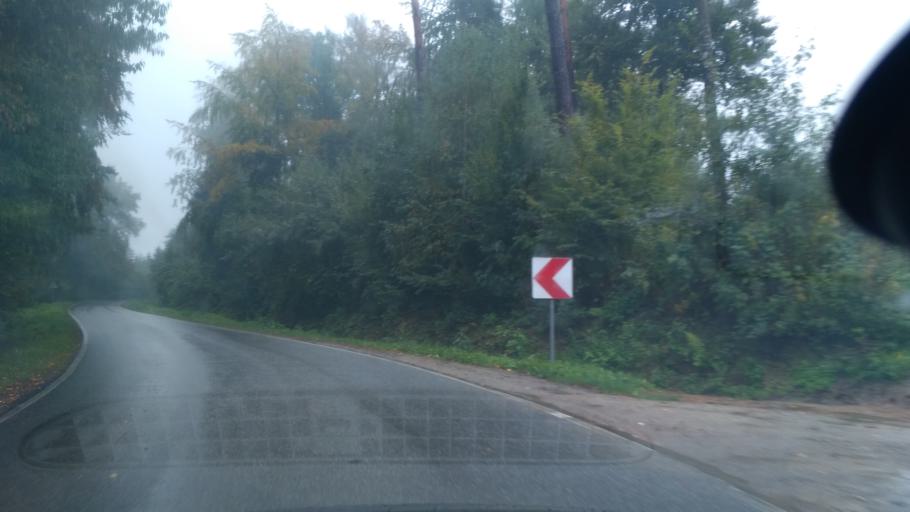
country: PL
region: Subcarpathian Voivodeship
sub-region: Powiat ropczycko-sedziszowski
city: Niedzwiada
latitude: 50.0485
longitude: 21.5328
